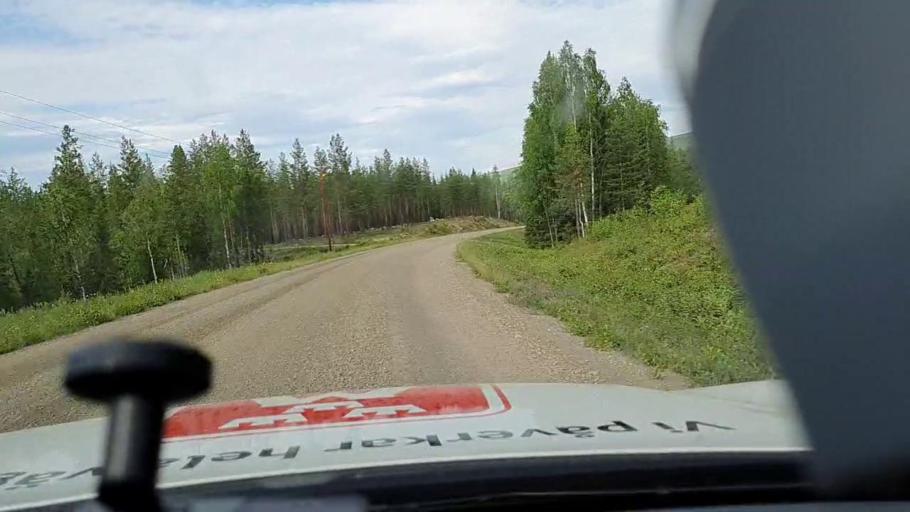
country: SE
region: Norrbotten
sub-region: Alvsbyns Kommun
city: AElvsbyn
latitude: 66.1367
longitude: 20.9986
